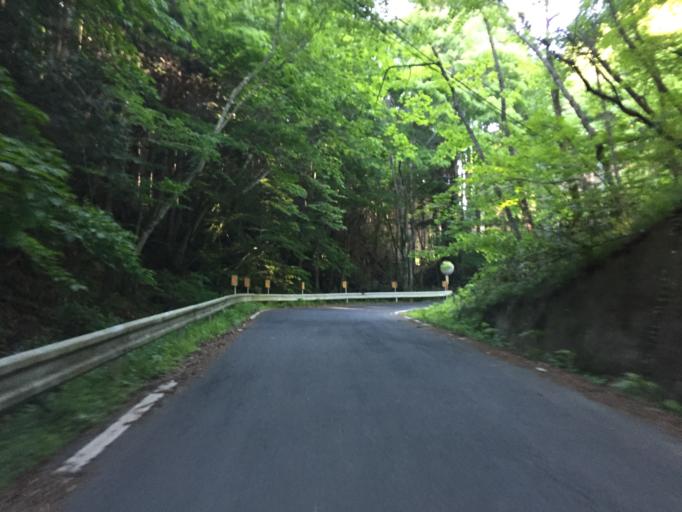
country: JP
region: Ibaraki
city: Kitaibaraki
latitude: 36.8959
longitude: 140.6202
